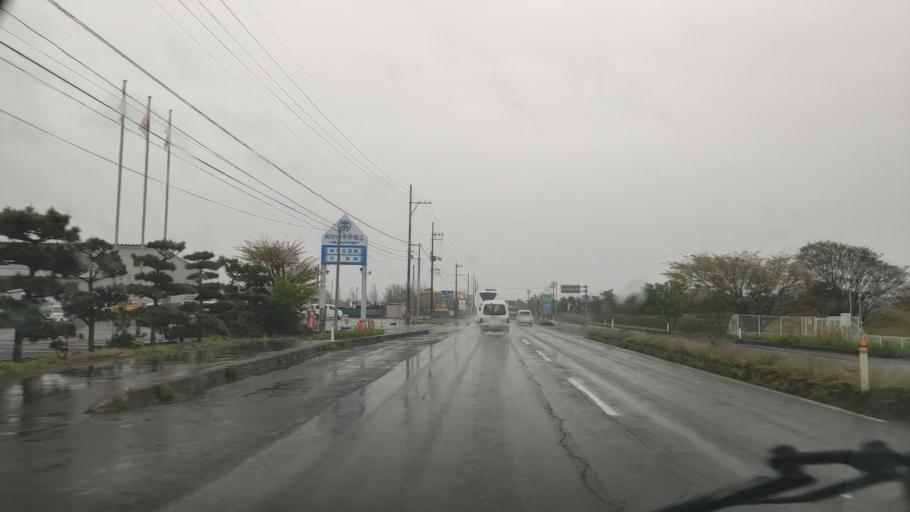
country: JP
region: Akita
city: Tenno
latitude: 39.8627
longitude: 140.0070
